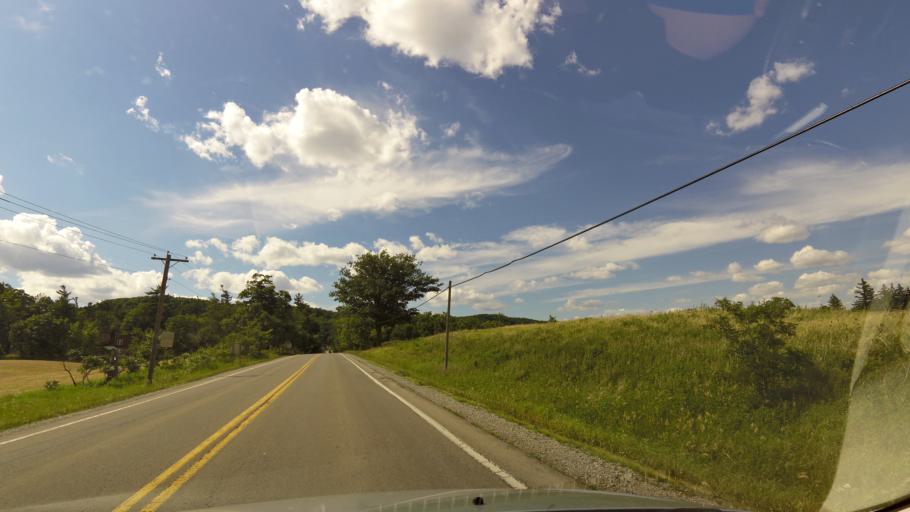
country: CA
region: Ontario
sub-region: Halton
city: Milton
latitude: 43.4642
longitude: -79.9011
